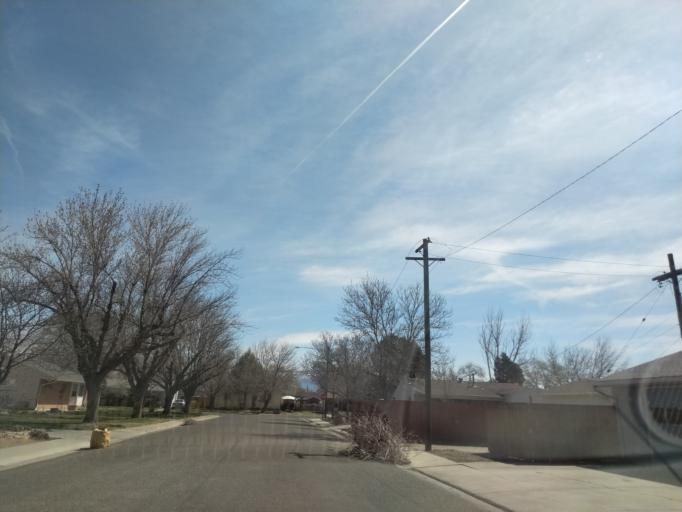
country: US
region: Colorado
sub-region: Mesa County
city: Grand Junction
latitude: 39.0801
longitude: -108.5405
